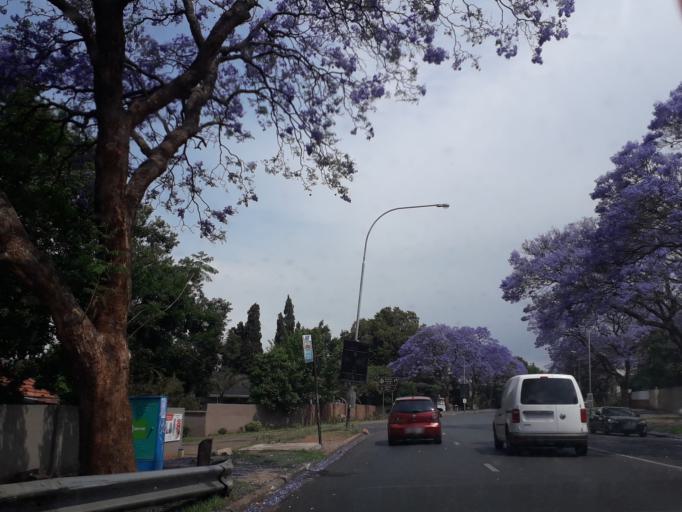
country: ZA
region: Gauteng
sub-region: City of Johannesburg Metropolitan Municipality
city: Johannesburg
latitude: -26.1659
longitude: 28.0140
